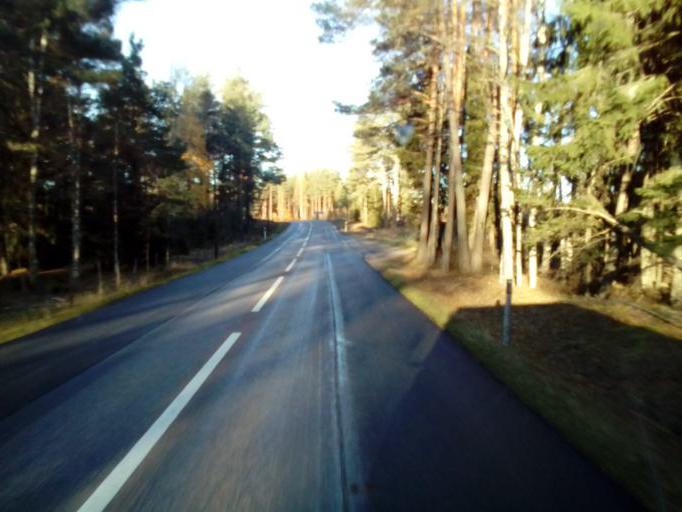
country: SE
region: OErebro
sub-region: Hallsbergs Kommun
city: Palsboda
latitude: 58.8310
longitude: 15.4089
